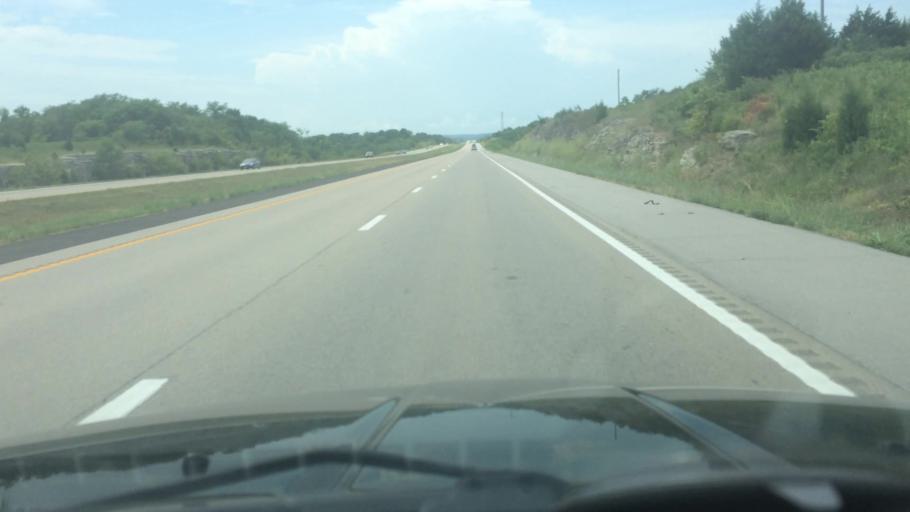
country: US
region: Missouri
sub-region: Polk County
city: Humansville
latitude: 37.7687
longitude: -93.5635
